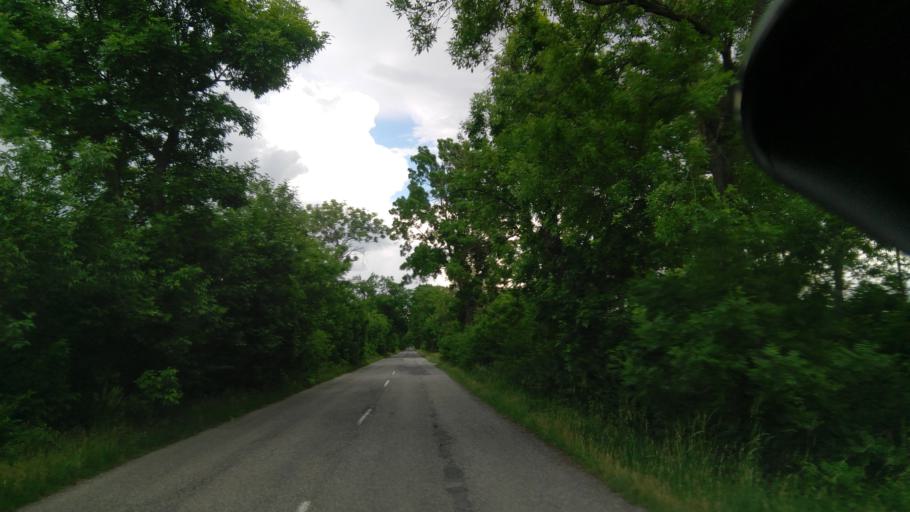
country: HU
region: Bekes
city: Bucsa
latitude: 47.1624
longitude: 21.0939
